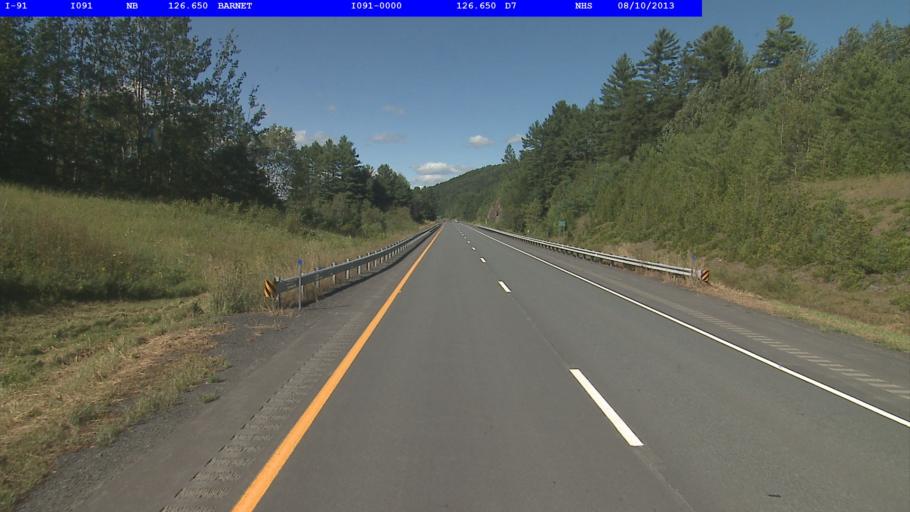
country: US
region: Vermont
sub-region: Caledonia County
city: Saint Johnsbury
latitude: 44.3739
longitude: -72.0220
